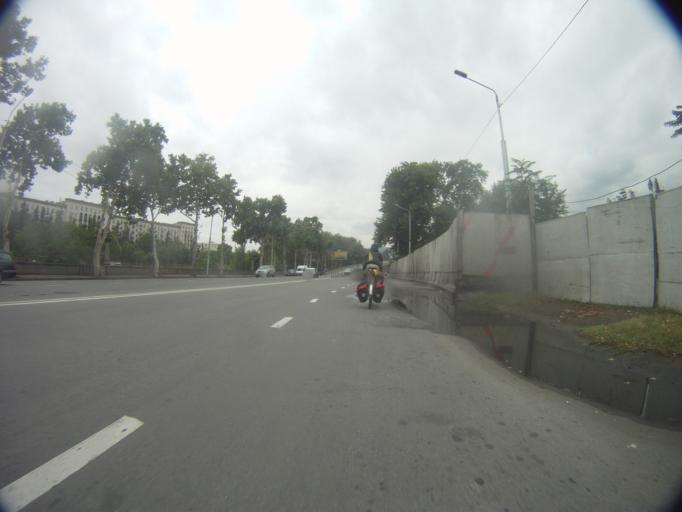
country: GE
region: T'bilisi
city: Tbilisi
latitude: 41.7186
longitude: 44.7853
